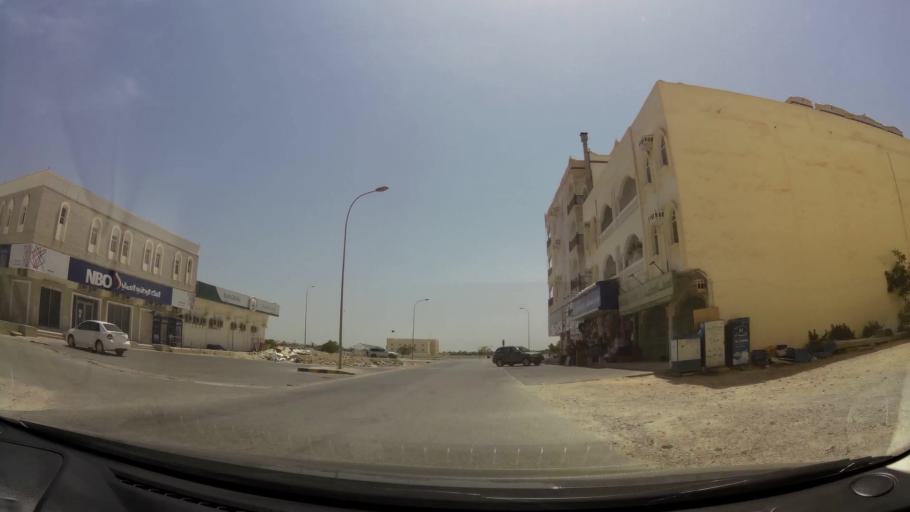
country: OM
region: Zufar
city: Salalah
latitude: 17.0521
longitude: 54.1500
